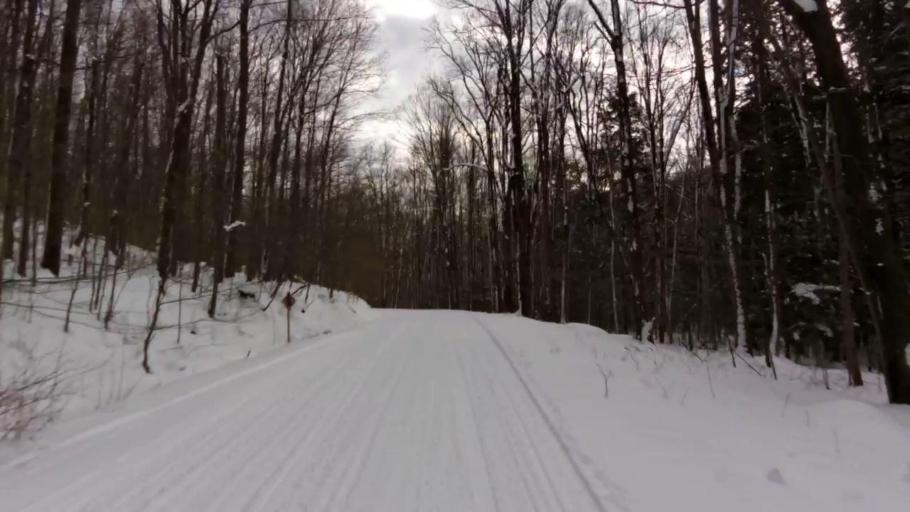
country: US
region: New York
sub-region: Cattaraugus County
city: Salamanca
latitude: 42.0516
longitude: -78.7527
